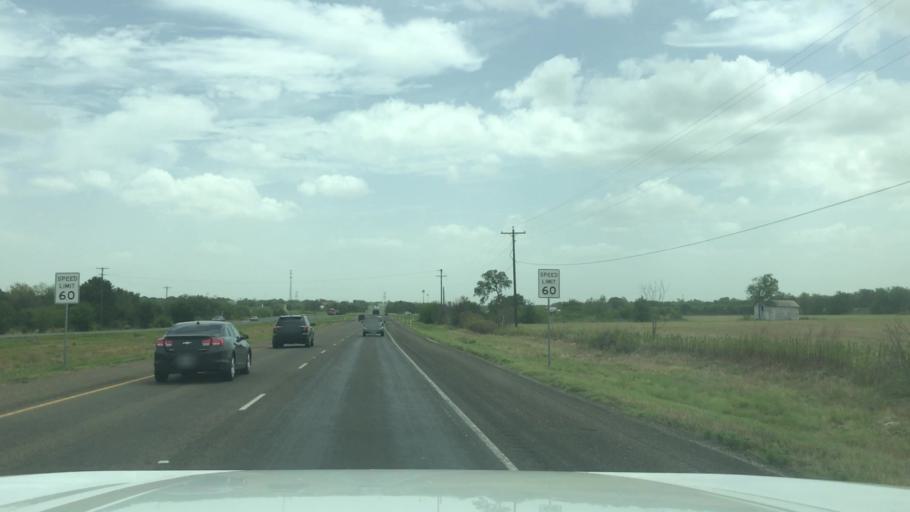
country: US
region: Texas
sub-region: McLennan County
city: Riesel
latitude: 31.4861
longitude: -96.9273
